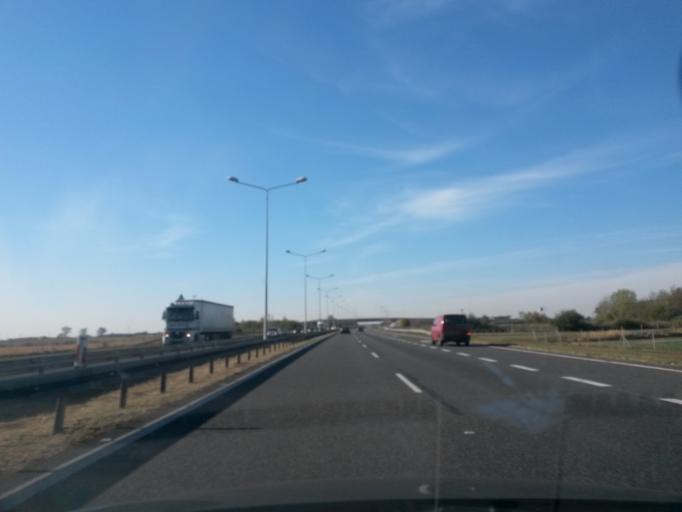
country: PL
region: Opole Voivodeship
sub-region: Powiat brzeski
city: Grodkow
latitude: 50.7785
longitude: 17.3555
